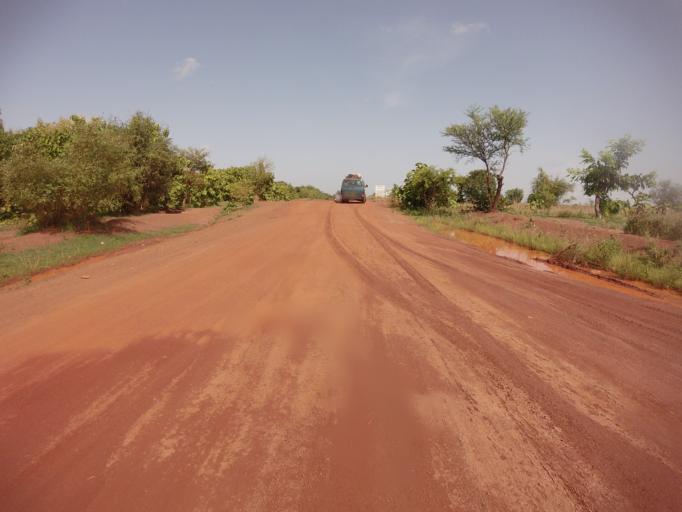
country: GH
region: Upper East
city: Bawku
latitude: 11.0024
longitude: -0.1970
